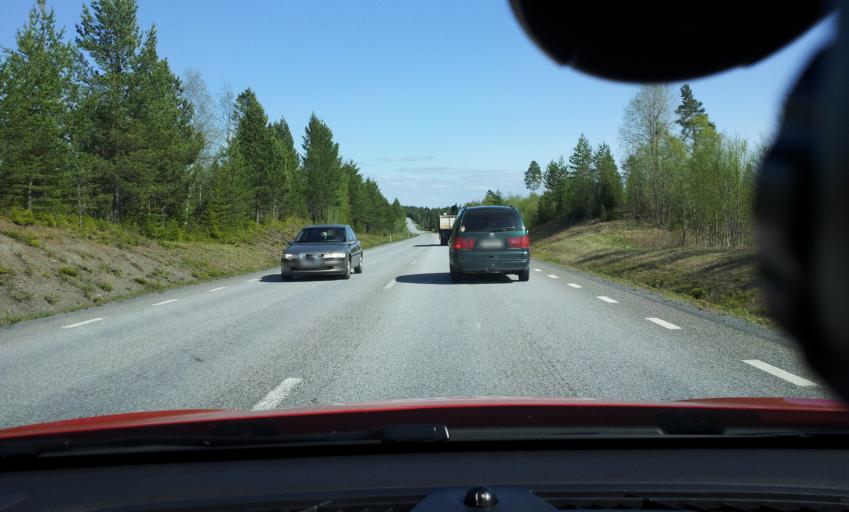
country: SE
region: Jaemtland
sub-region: Krokoms Kommun
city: Valla
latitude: 63.3079
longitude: 13.8144
